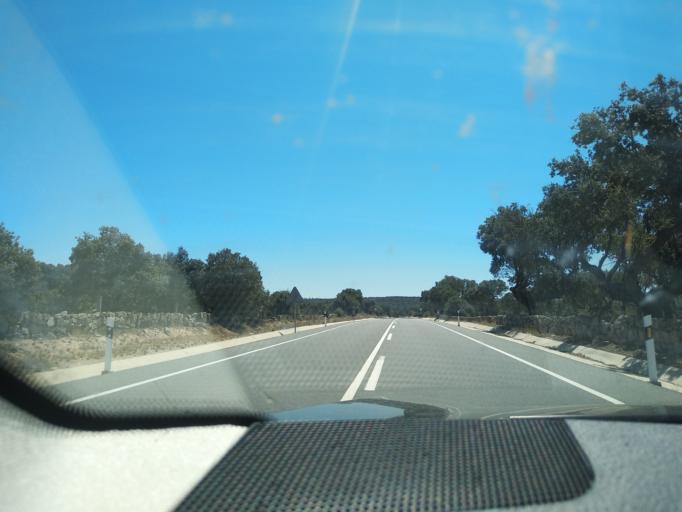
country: ES
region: Castille and Leon
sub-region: Provincia de Avila
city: Mingorria
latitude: 40.7029
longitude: -4.6709
